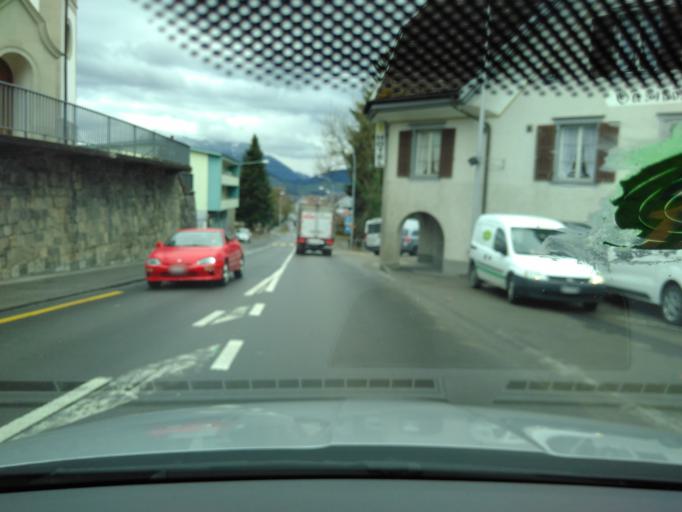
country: CH
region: Lucerne
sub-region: Hochdorf District
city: Ballwil
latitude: 47.1325
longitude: 8.3201
